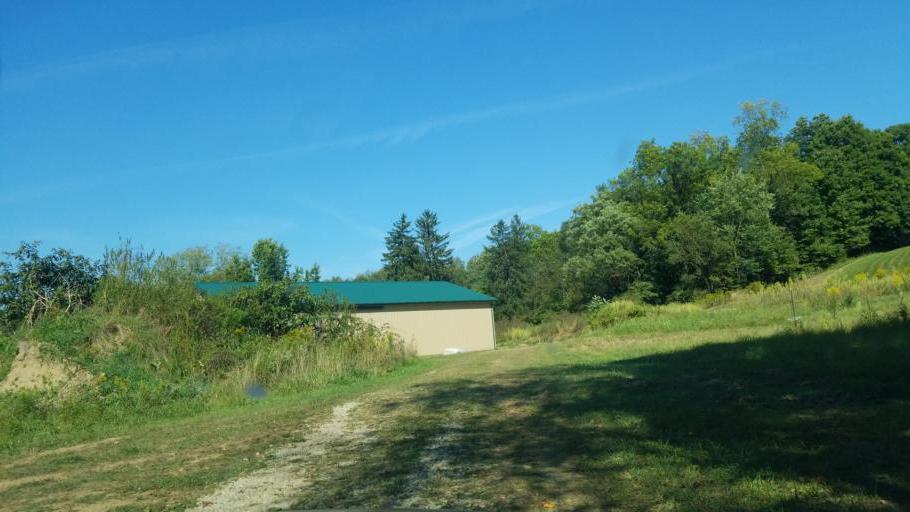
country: US
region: Ohio
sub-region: Sandusky County
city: Bellville
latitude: 40.6405
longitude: -82.4109
